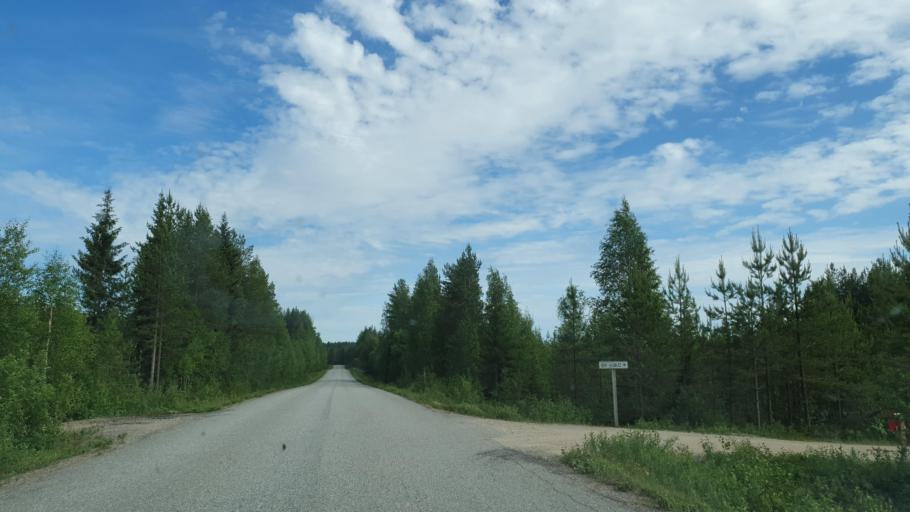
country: FI
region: Kainuu
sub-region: Kehys-Kainuu
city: Suomussalmi
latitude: 64.5547
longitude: 29.1646
